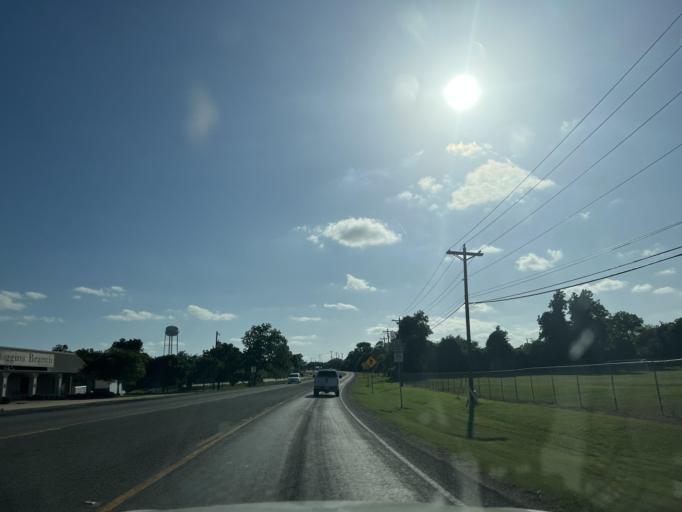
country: US
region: Texas
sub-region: Washington County
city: Brenham
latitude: 30.1772
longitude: -96.3958
